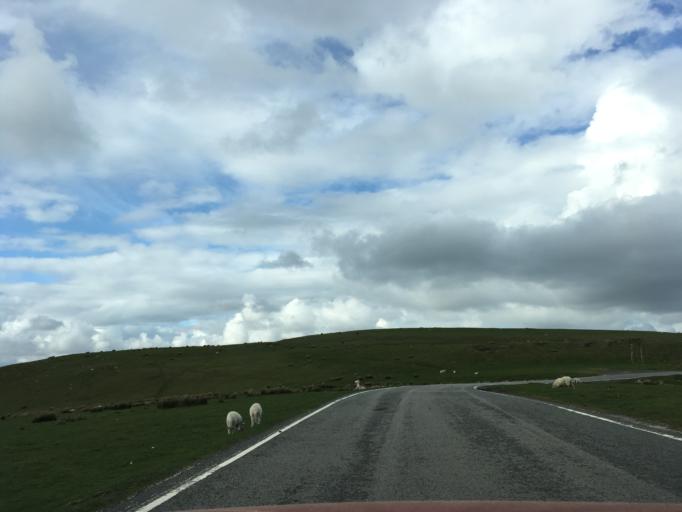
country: GB
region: Wales
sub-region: Caerphilly County Borough
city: Rhymney
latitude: 51.7183
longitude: -3.3070
